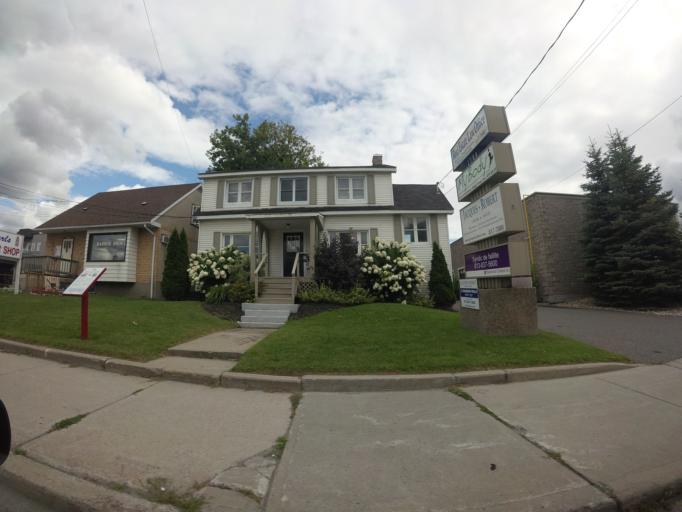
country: CA
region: Quebec
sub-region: Outaouais
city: Gatineau
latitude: 45.4731
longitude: -75.5209
